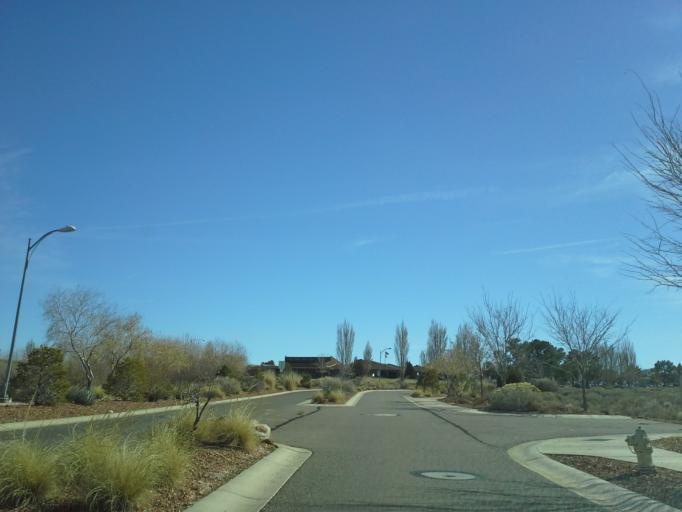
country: US
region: Arizona
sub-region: Coconino County
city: Page
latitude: 36.9330
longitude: -111.4621
